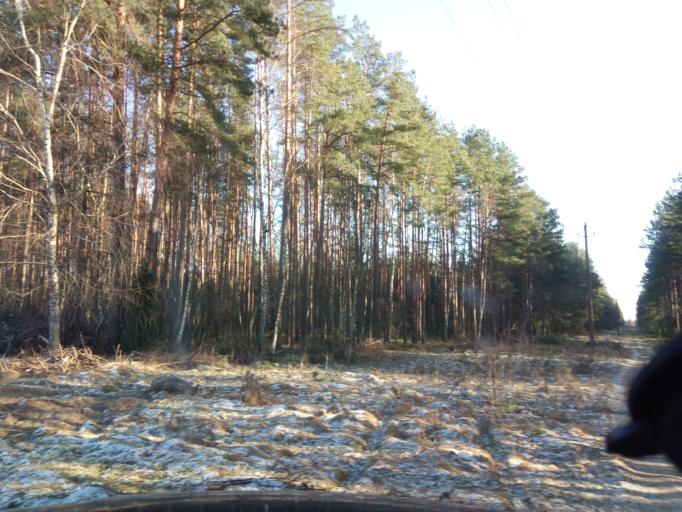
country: LT
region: Alytaus apskritis
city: Druskininkai
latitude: 53.9811
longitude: 23.8980
